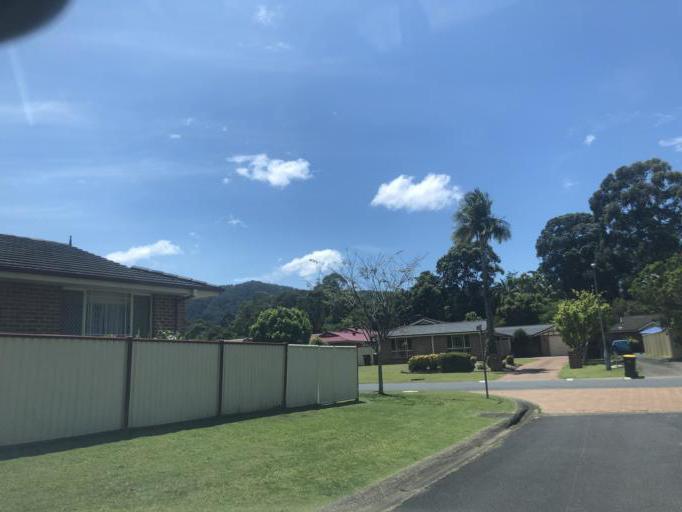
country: AU
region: New South Wales
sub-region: Coffs Harbour
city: Coffs Harbour
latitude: -30.2891
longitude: 153.0962
